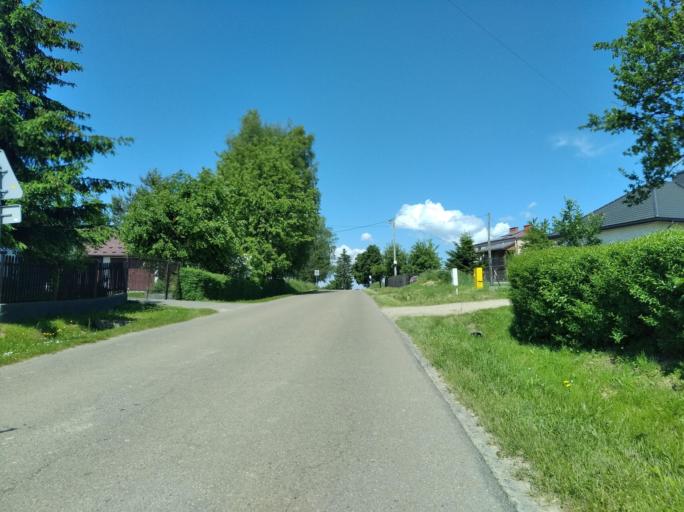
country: PL
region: Subcarpathian Voivodeship
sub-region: Powiat jasielski
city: Tarnowiec
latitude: 49.7207
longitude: 21.5997
